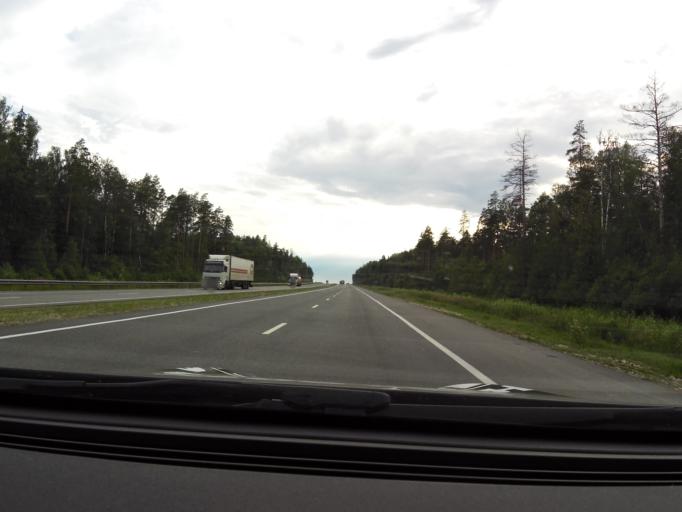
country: RU
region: Vladimir
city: Kommunar
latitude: 56.0904
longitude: 40.5134
